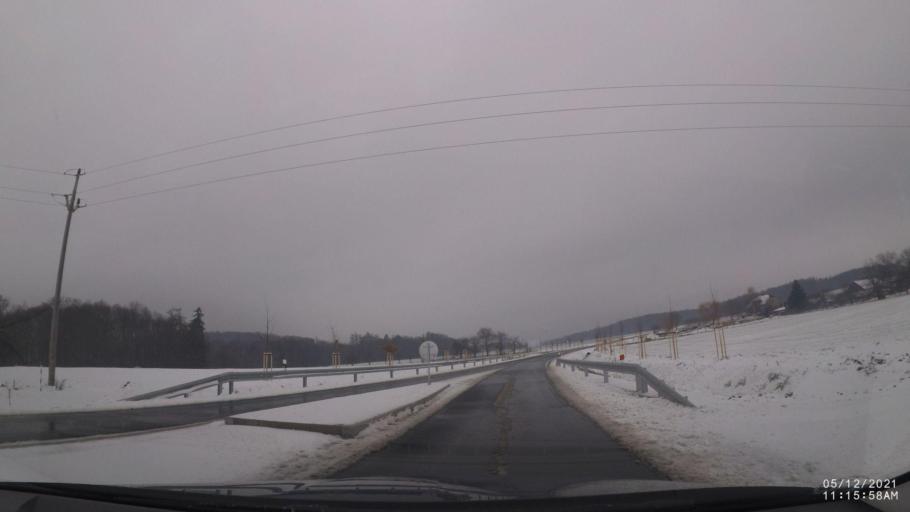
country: CZ
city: Solnice
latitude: 50.1829
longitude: 16.2199
